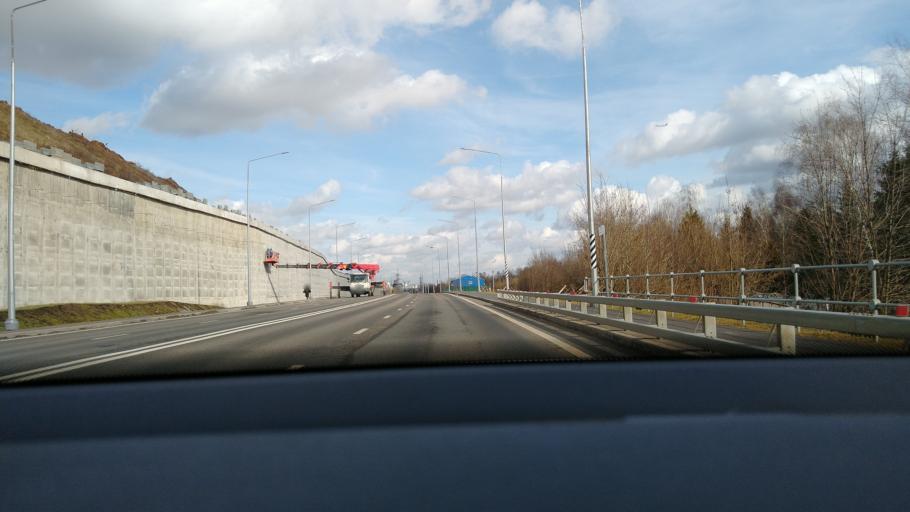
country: RU
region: Moskovskaya
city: Mosrentgen
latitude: 55.6097
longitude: 37.4337
